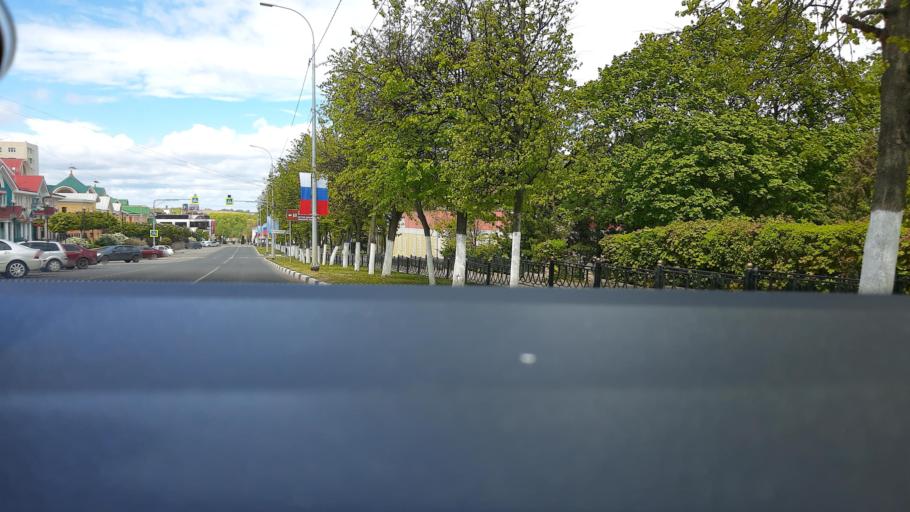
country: RU
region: Moskovskaya
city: Dmitrov
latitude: 56.3419
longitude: 37.5227
